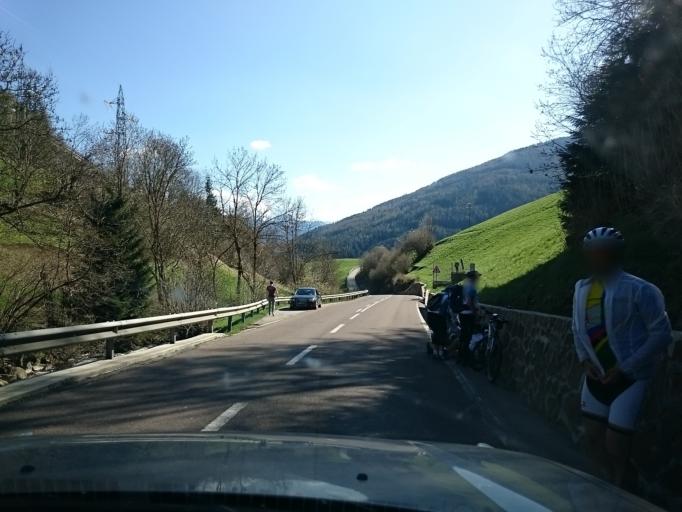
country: IT
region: Trentino-Alto Adige
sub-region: Bolzano
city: Colle Isarco
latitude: 46.9439
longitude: 11.4488
